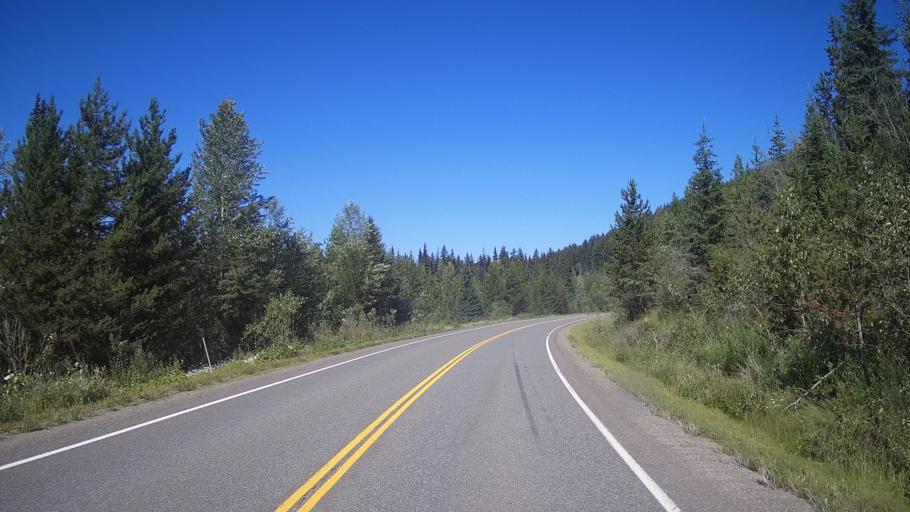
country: CA
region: British Columbia
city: Kamloops
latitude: 51.4956
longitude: -120.4155
